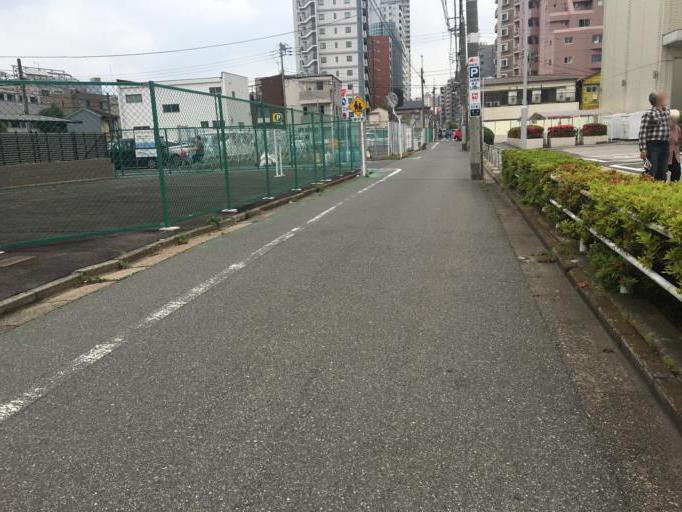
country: JP
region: Saitama
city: Soka
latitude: 35.7357
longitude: 139.7853
